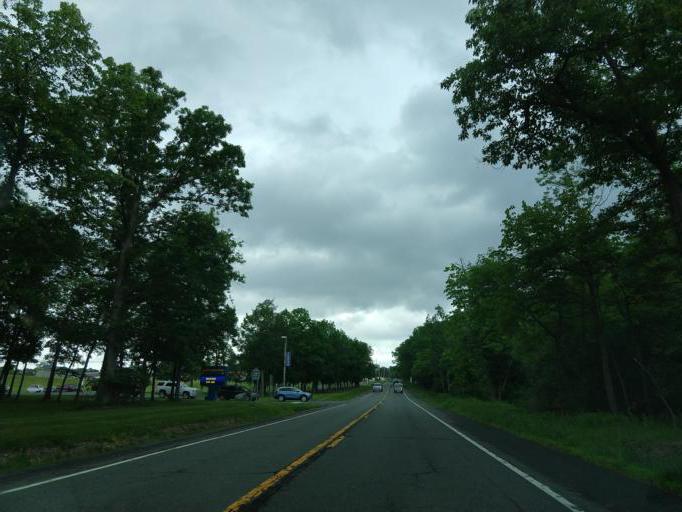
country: US
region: New York
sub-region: Tompkins County
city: Northwest Ithaca
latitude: 42.5424
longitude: -76.5342
